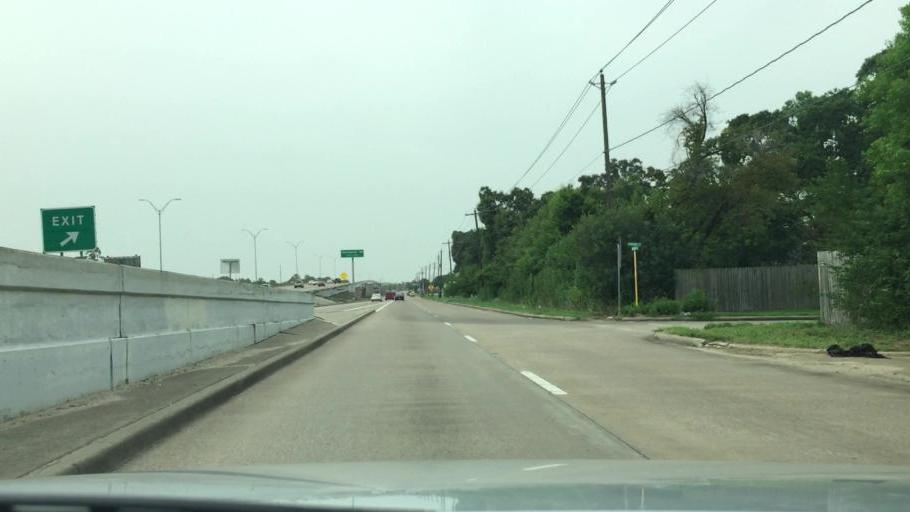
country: US
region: Texas
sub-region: Harris County
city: Cloverleaf
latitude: 29.7865
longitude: -95.1591
